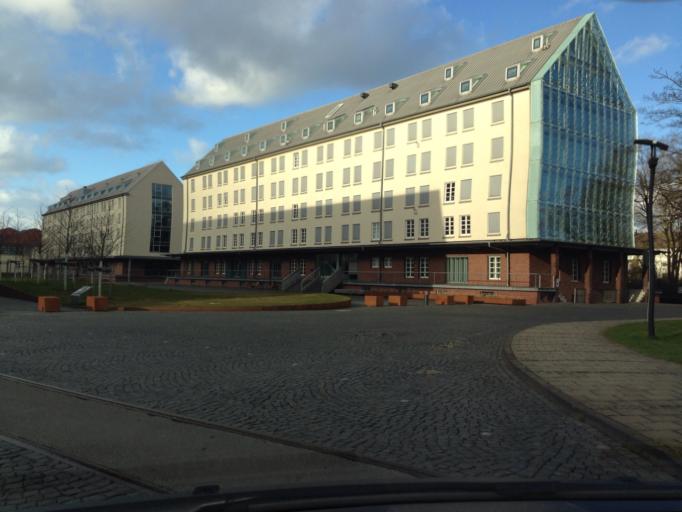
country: DE
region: North Rhine-Westphalia
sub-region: Regierungsbezirk Munster
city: Muenster
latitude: 51.9965
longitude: 7.6347
